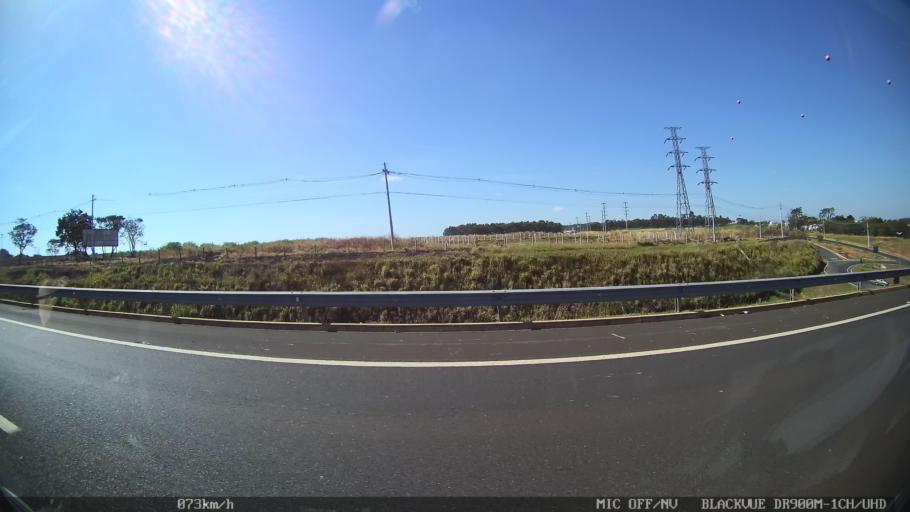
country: BR
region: Sao Paulo
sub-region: Franca
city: Franca
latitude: -20.4776
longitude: -47.4113
